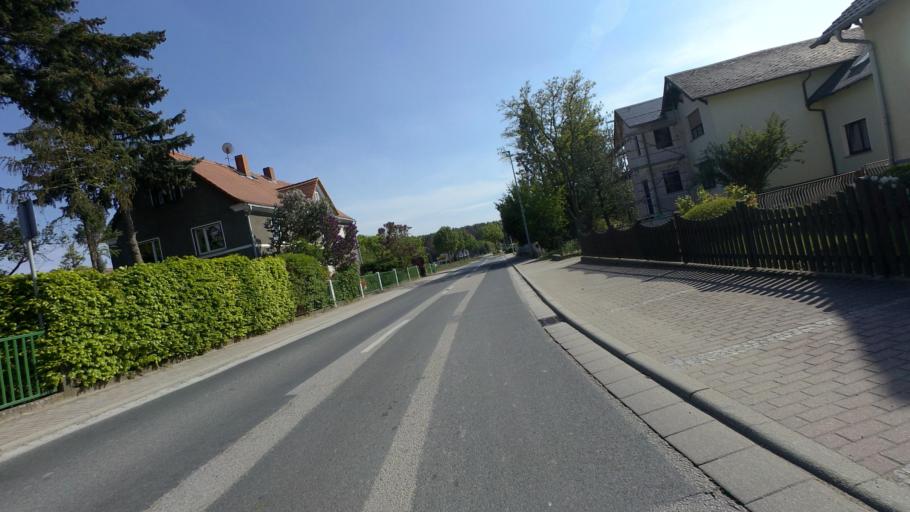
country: DE
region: Saxony
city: Ossling
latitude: 51.3588
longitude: 14.1666
